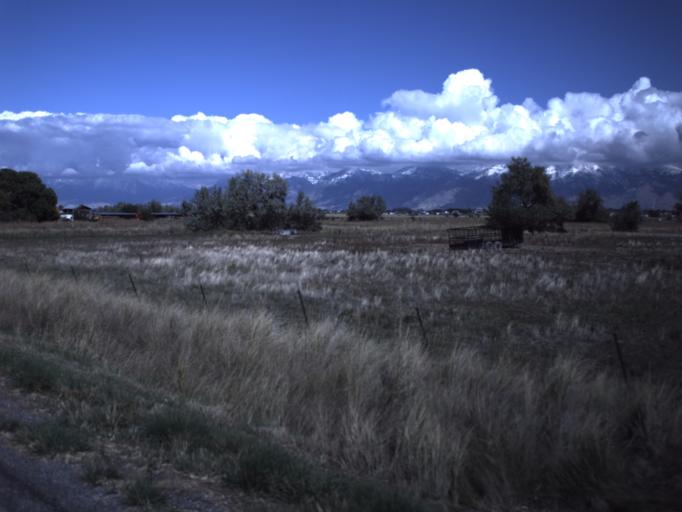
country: US
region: Utah
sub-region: Utah County
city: West Mountain
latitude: 40.0799
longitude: -111.7878
